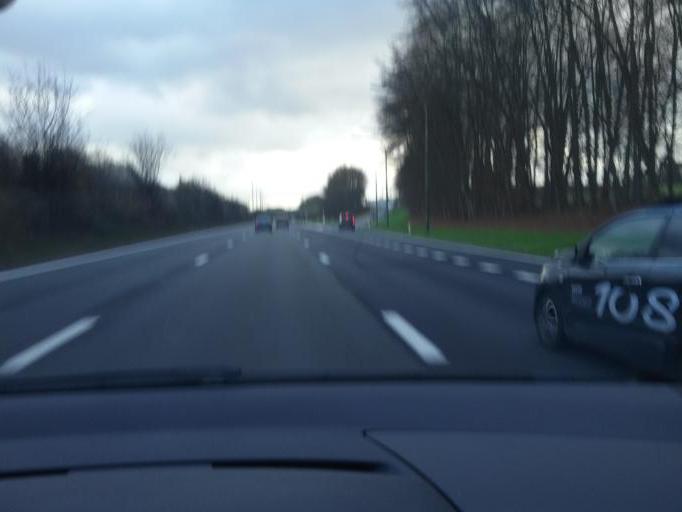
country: BE
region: Flanders
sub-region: Provincie Vlaams-Brabant
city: Overijse
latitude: 50.7559
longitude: 4.5217
